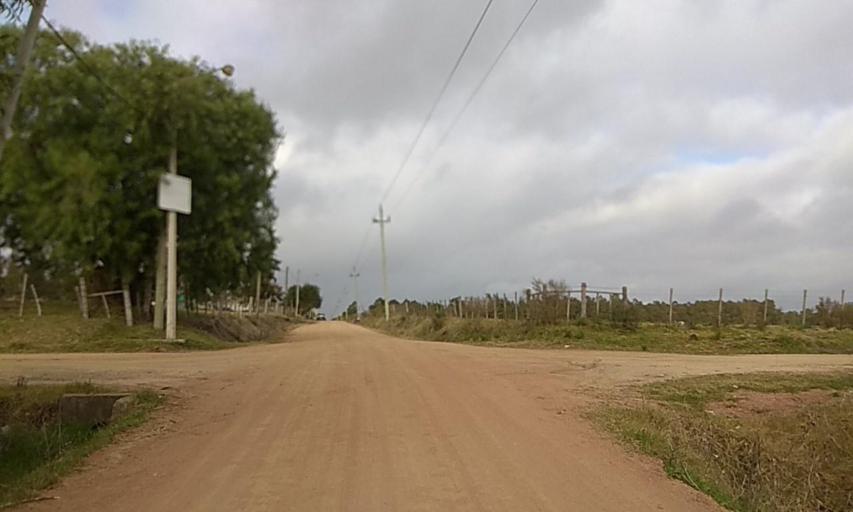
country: UY
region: Florida
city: Florida
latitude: -34.0685
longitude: -56.2197
